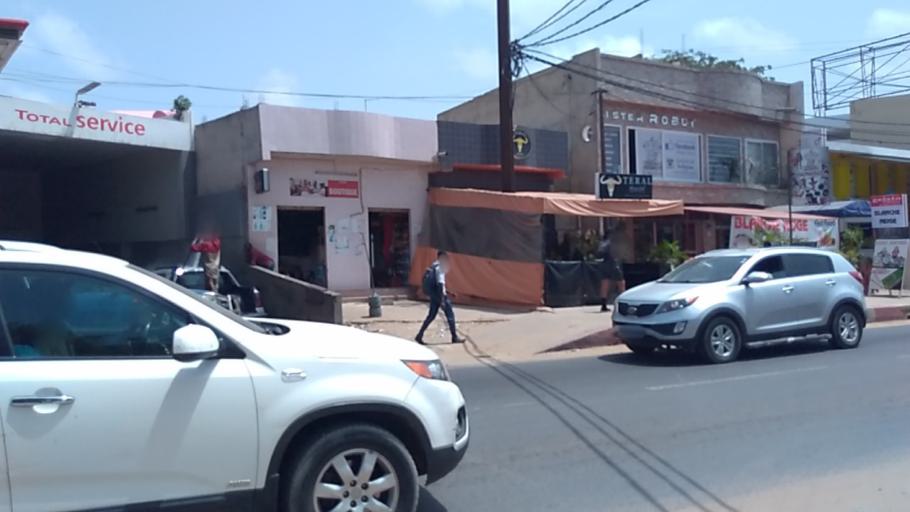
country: SN
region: Dakar
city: Mermoz Boabab
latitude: 14.7182
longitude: -17.4877
